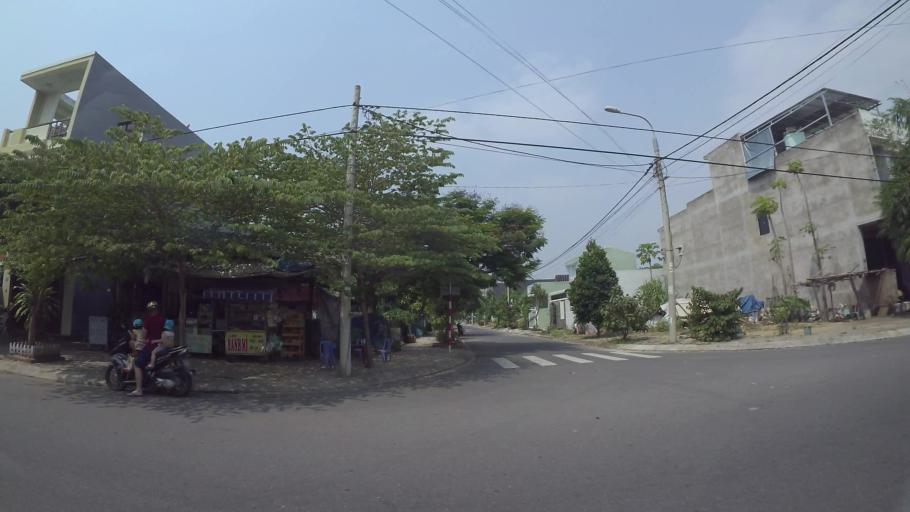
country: VN
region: Da Nang
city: Cam Le
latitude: 15.9921
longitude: 108.2135
